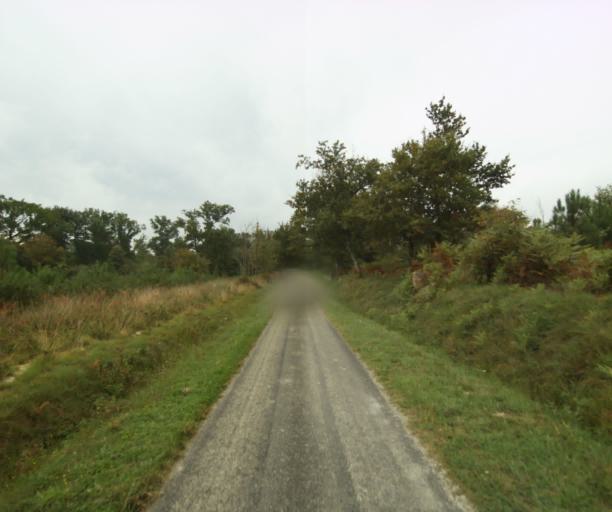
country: FR
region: Midi-Pyrenees
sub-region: Departement du Gers
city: Cazaubon
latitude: 43.9230
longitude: -0.1805
